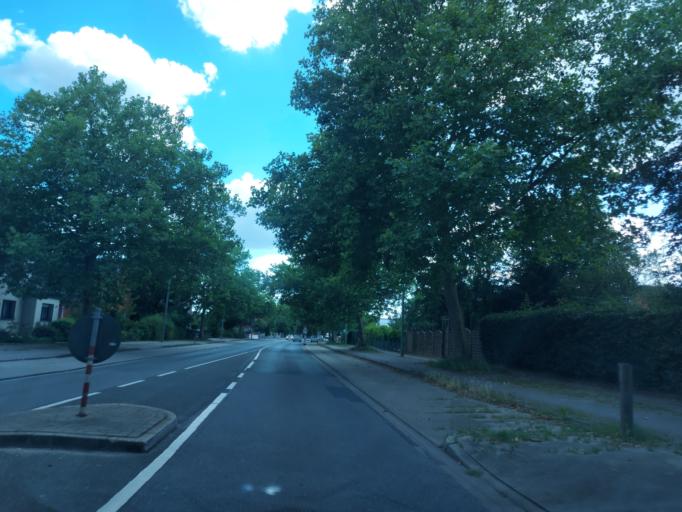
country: DE
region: Lower Saxony
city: Georgsmarienhutte
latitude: 52.2385
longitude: 8.0299
